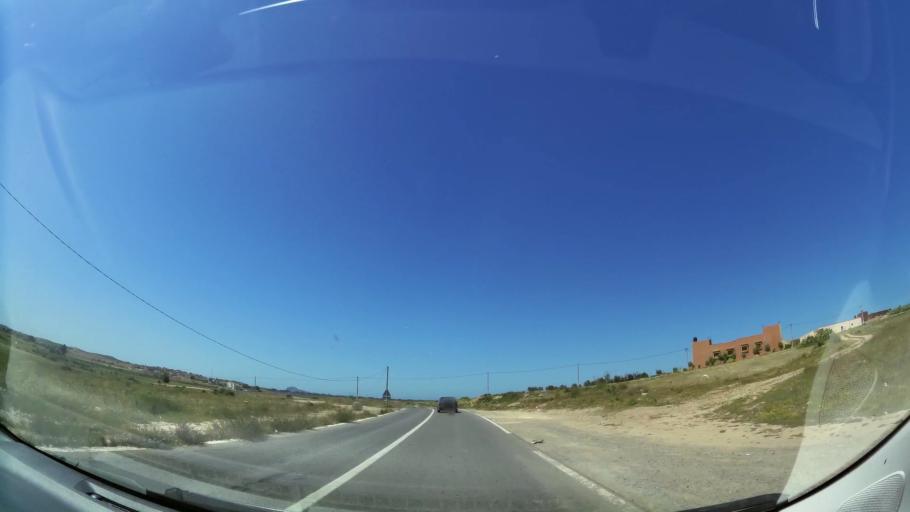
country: MA
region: Oriental
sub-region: Berkane-Taourirt
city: Madagh
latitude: 35.1114
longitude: -2.3630
